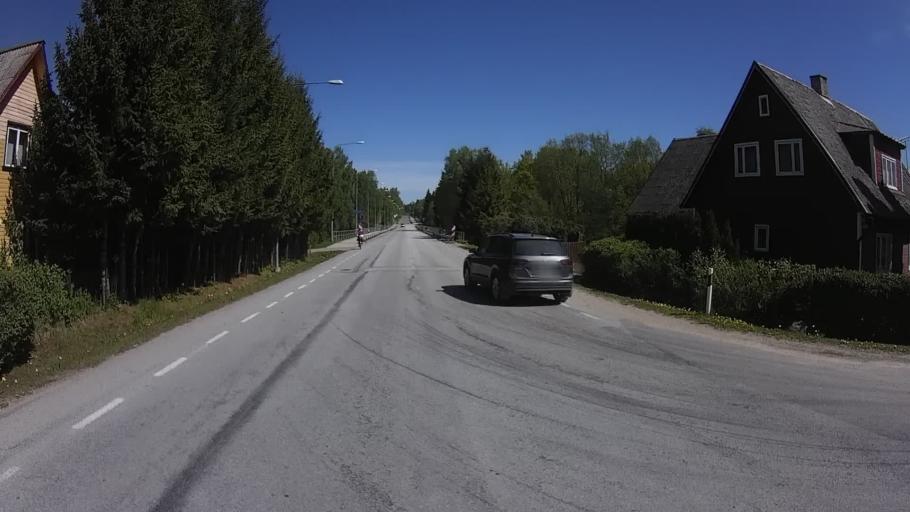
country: EE
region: Polvamaa
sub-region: Raepina vald
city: Rapina
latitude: 58.0911
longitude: 27.4573
